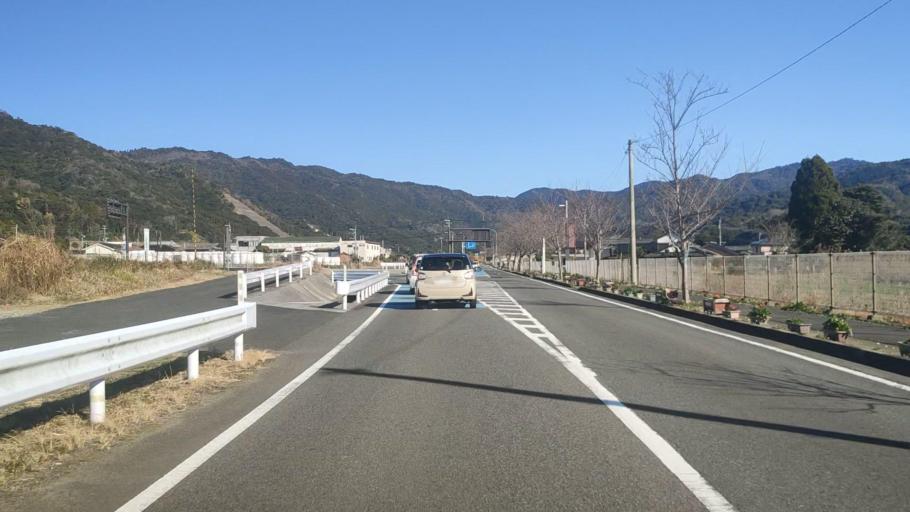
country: JP
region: Miyazaki
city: Nobeoka
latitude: 32.7095
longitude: 131.8197
